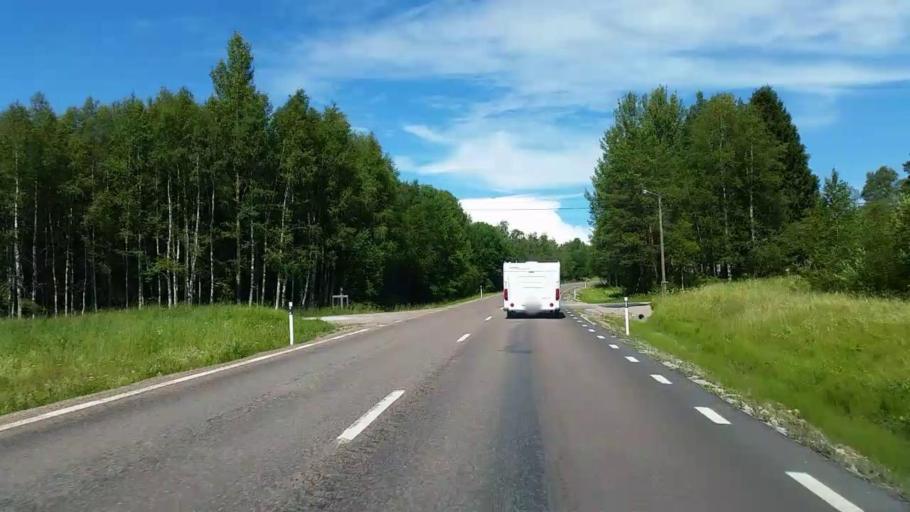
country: SE
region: Dalarna
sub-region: Rattviks Kommun
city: Raettvik
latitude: 60.9934
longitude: 15.2173
